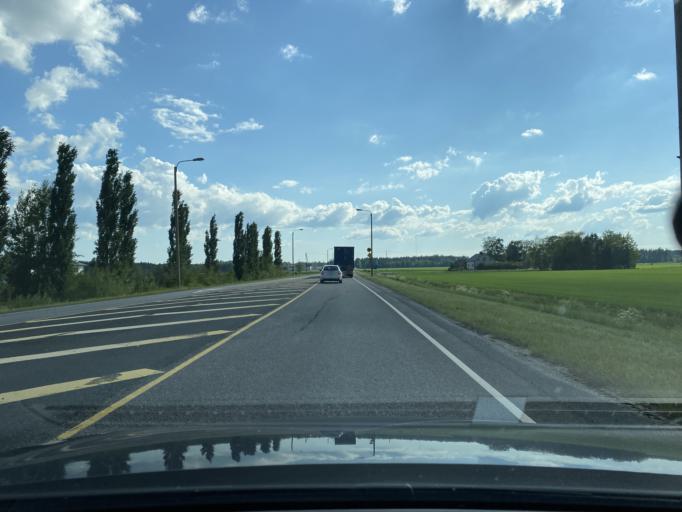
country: FI
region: Varsinais-Suomi
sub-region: Loimaa
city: Mellilae
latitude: 60.7932
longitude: 22.9039
